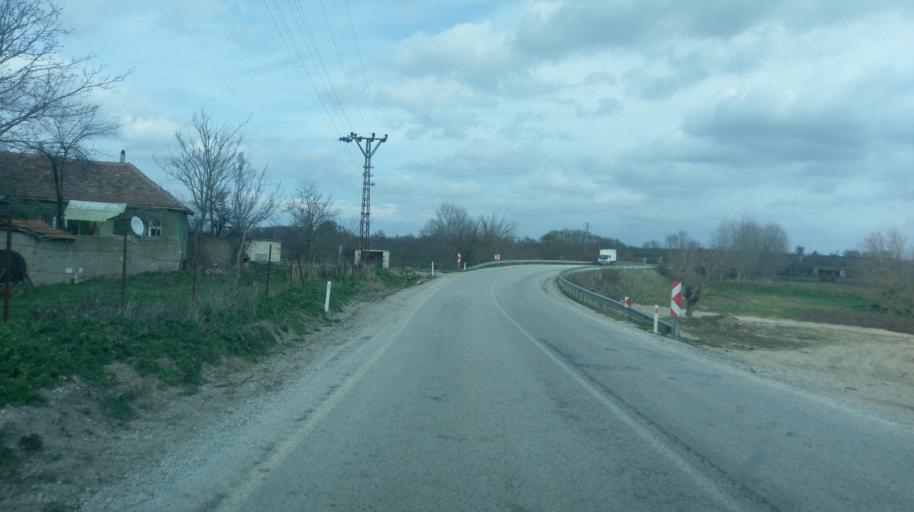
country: TR
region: Kirklareli
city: Inece
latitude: 41.6717
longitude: 26.9895
